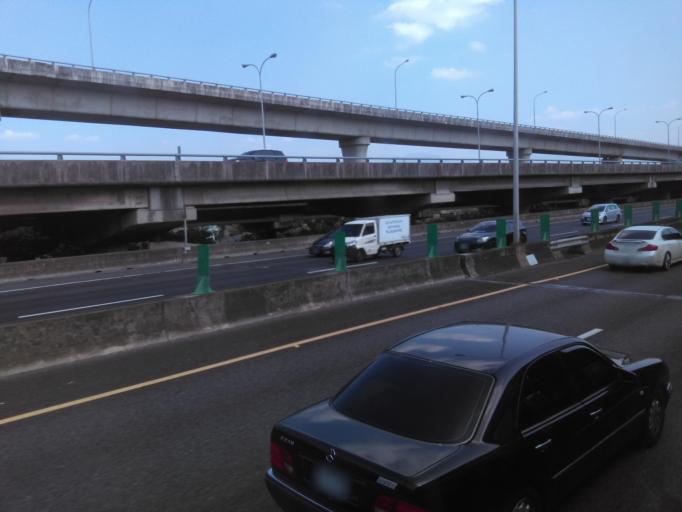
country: TW
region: Taipei
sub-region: Taipei
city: Banqiao
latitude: 25.0706
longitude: 121.4452
